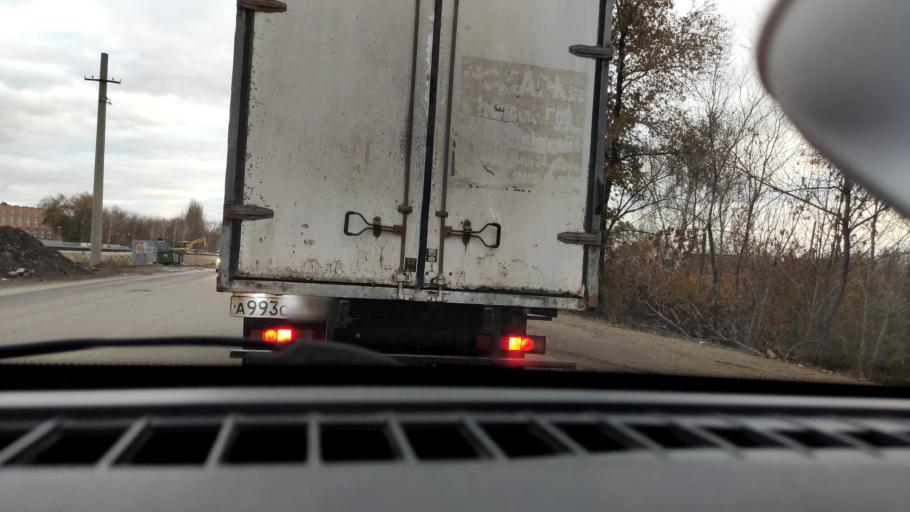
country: RU
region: Samara
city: Samara
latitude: 53.1413
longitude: 50.0997
